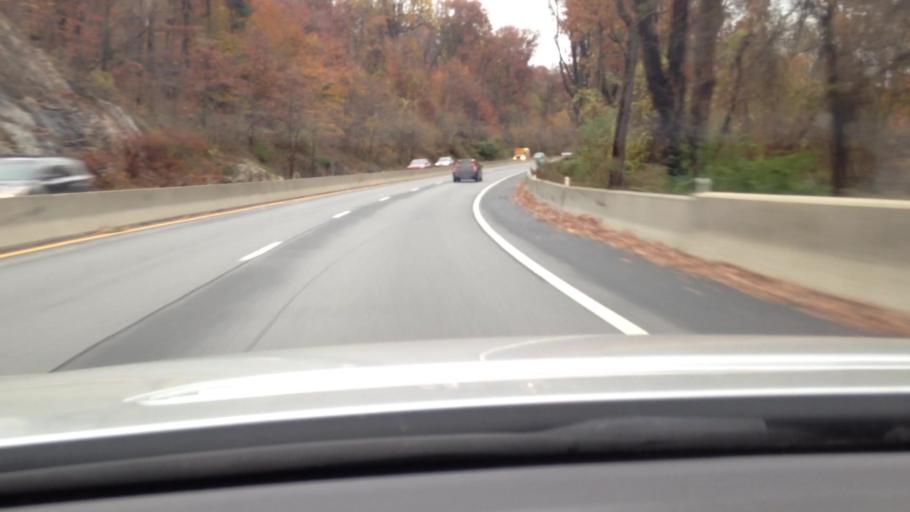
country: US
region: New York
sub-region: Westchester County
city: Tarrytown
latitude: 41.0769
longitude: -73.8339
